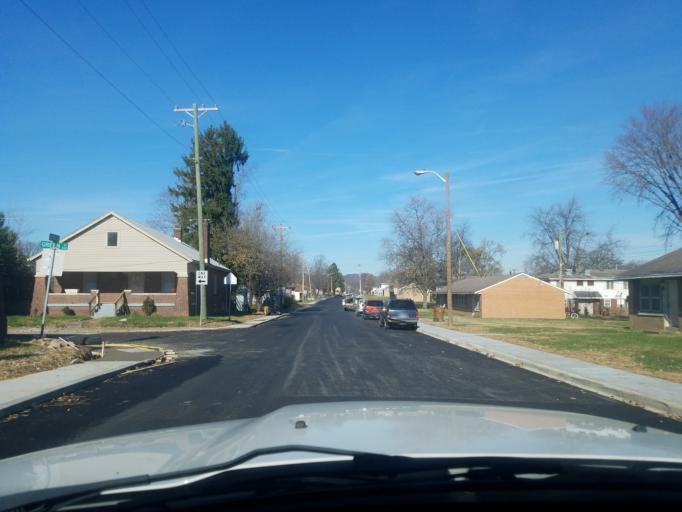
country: US
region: Indiana
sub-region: Floyd County
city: New Albany
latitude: 38.2980
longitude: -85.8278
